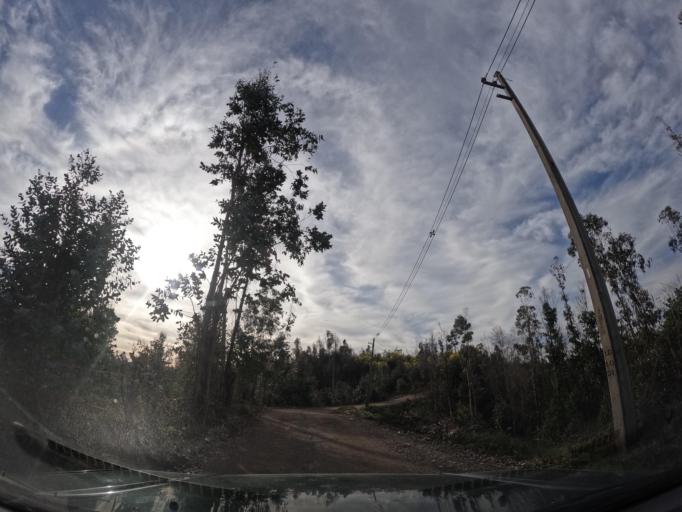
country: CL
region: Biobio
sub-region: Provincia de Concepcion
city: Chiguayante
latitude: -37.0283
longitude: -72.9055
